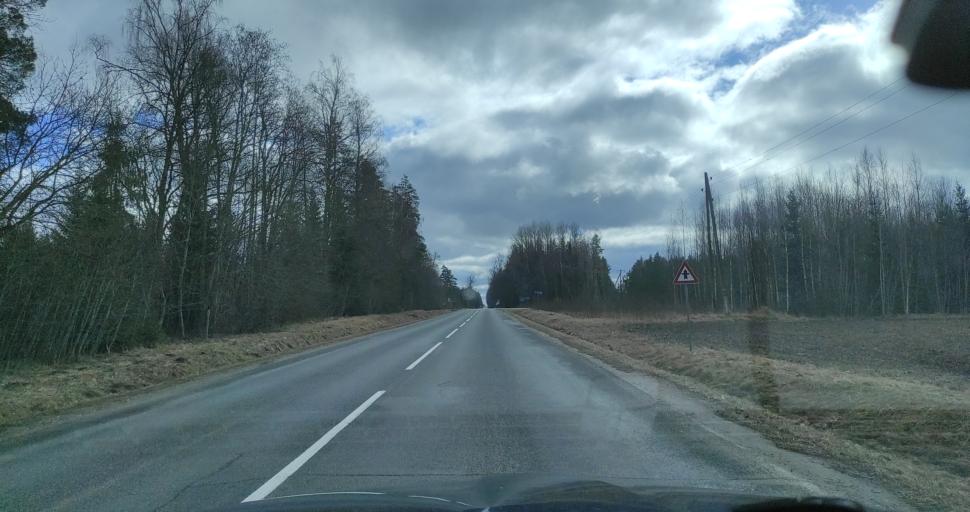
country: LV
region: Talsu Rajons
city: Stende
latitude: 57.1266
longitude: 22.5382
